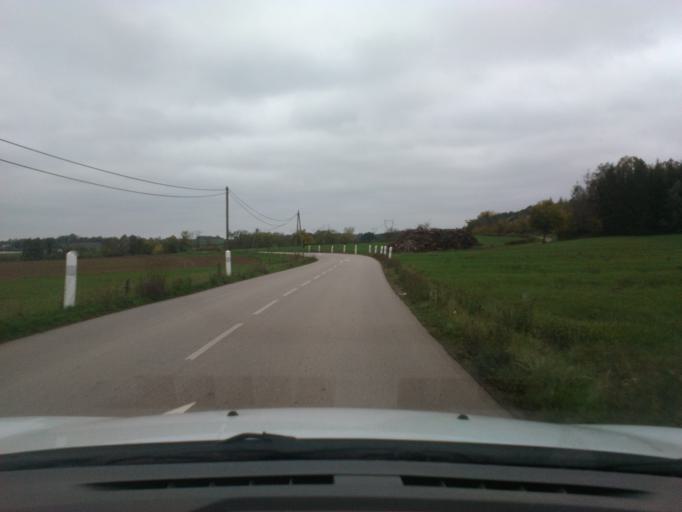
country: FR
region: Lorraine
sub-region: Departement des Vosges
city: Deyvillers
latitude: 48.2597
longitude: 6.5310
